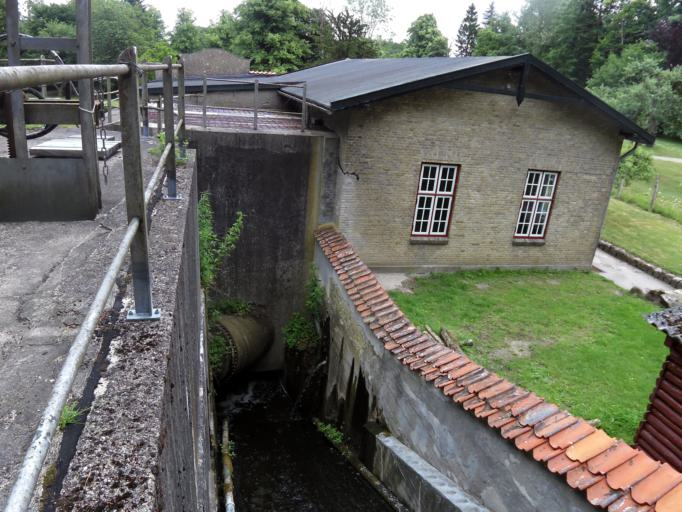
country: DK
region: South Denmark
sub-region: Haderslev Kommune
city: Vojens
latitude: 55.2331
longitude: 9.3872
